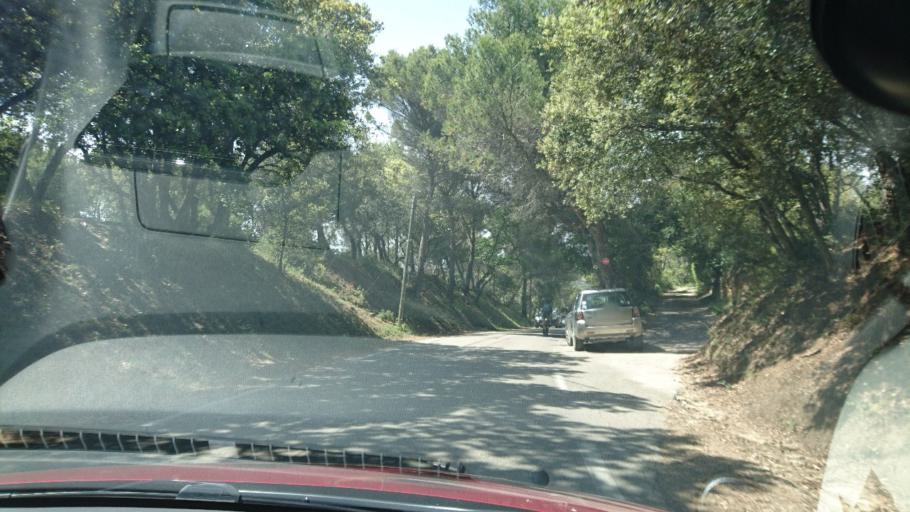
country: FR
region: Provence-Alpes-Cote d'Azur
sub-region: Departement du Vaucluse
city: Bedoin
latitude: 44.1341
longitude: 5.1673
